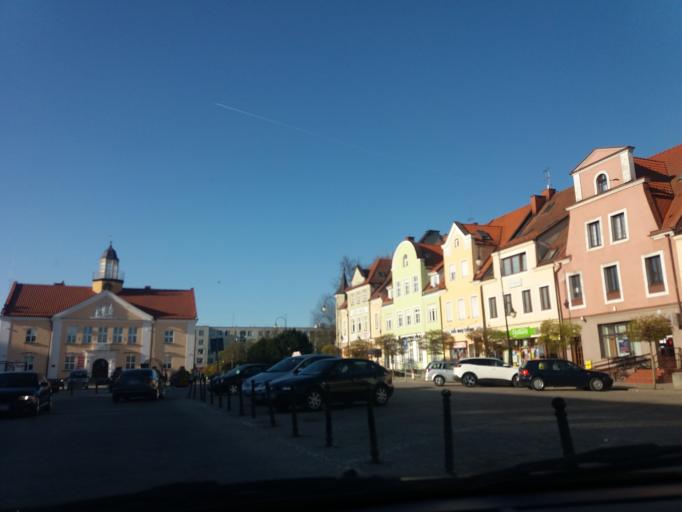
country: PL
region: Warmian-Masurian Voivodeship
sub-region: Powiat nidzicki
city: Nidzica
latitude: 53.3590
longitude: 20.4258
